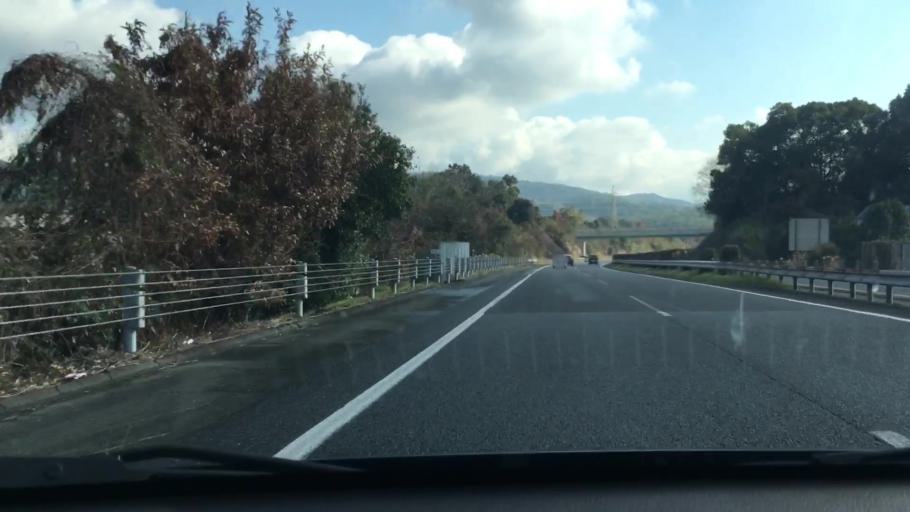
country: JP
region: Kumamoto
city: Matsubase
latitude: 32.6390
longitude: 130.7082
